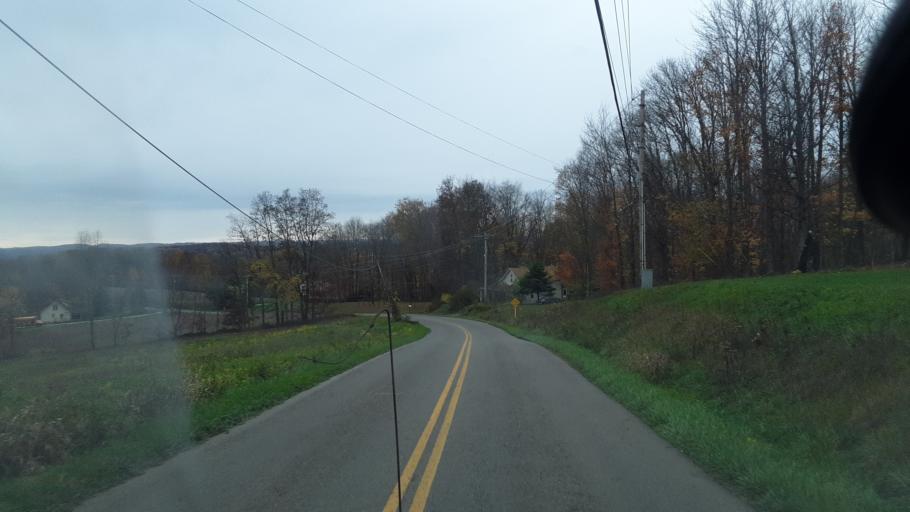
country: US
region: Ohio
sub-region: Holmes County
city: Millersburg
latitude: 40.4905
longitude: -81.9672
